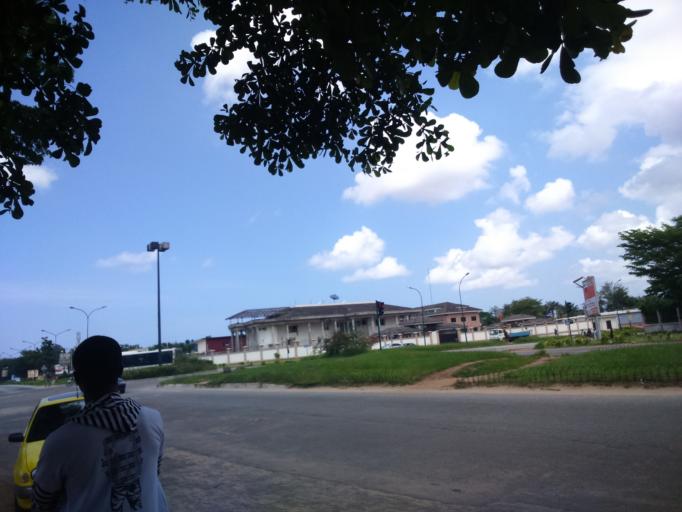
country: CI
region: Lagunes
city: Abidjan
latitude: 5.3445
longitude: -4.0028
